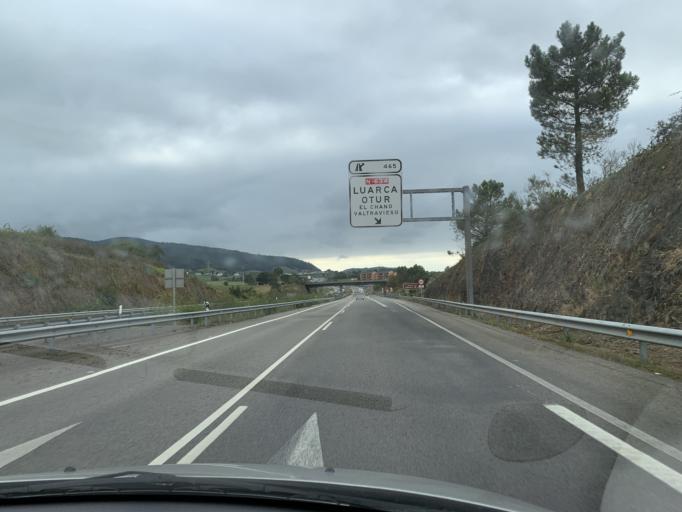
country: ES
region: Asturias
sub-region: Province of Asturias
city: Navia
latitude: 43.5267
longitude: -6.5477
